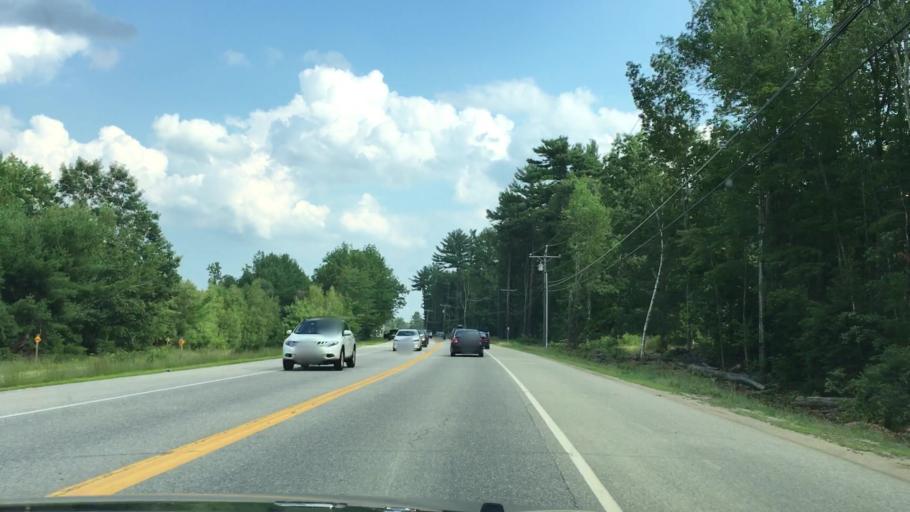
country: US
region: New Hampshire
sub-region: Strafford County
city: Farmington
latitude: 43.3481
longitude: -71.0245
